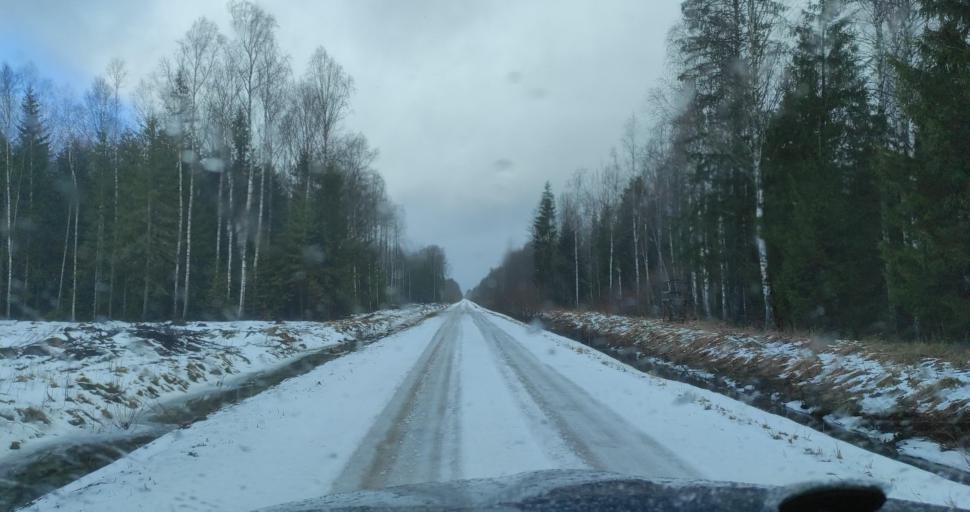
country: LV
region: Dundaga
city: Dundaga
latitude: 57.3926
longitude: 22.1270
